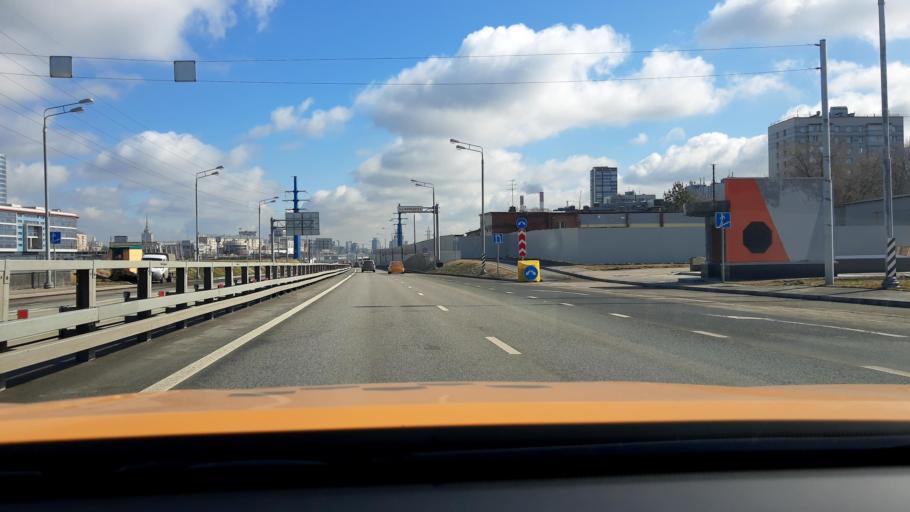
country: RU
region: Moscow
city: Vorob'yovo
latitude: 55.7325
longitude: 37.5289
